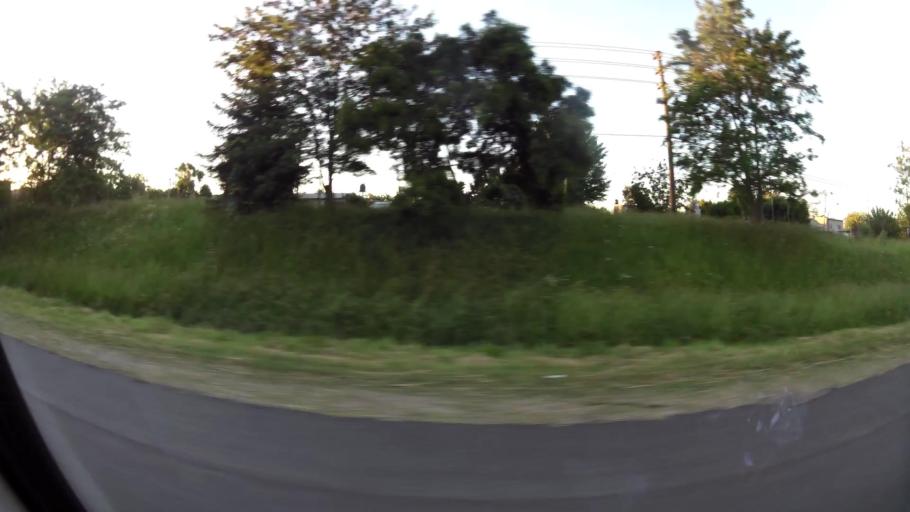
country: AR
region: Buenos Aires
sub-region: Partido de Quilmes
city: Quilmes
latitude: -34.8119
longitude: -58.1775
